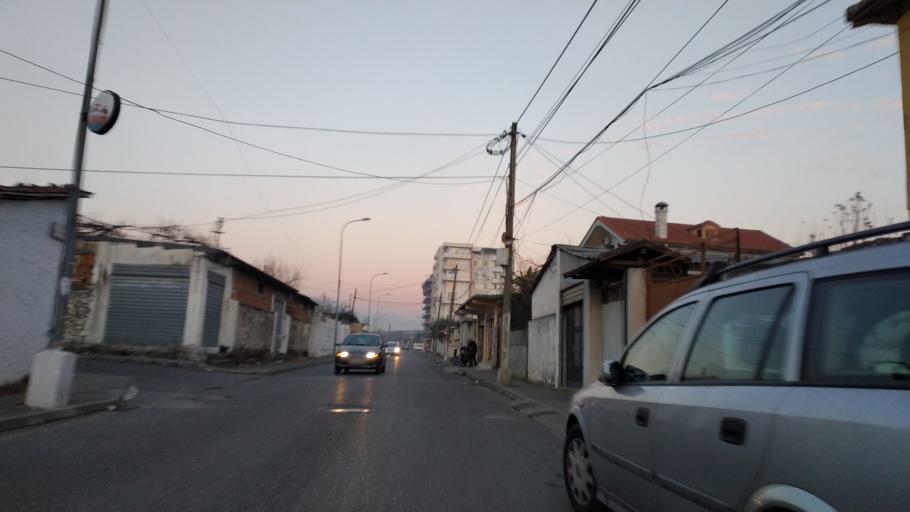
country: AL
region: Shkoder
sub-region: Rrethi i Shkodres
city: Shkoder
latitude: 42.0769
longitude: 19.5191
